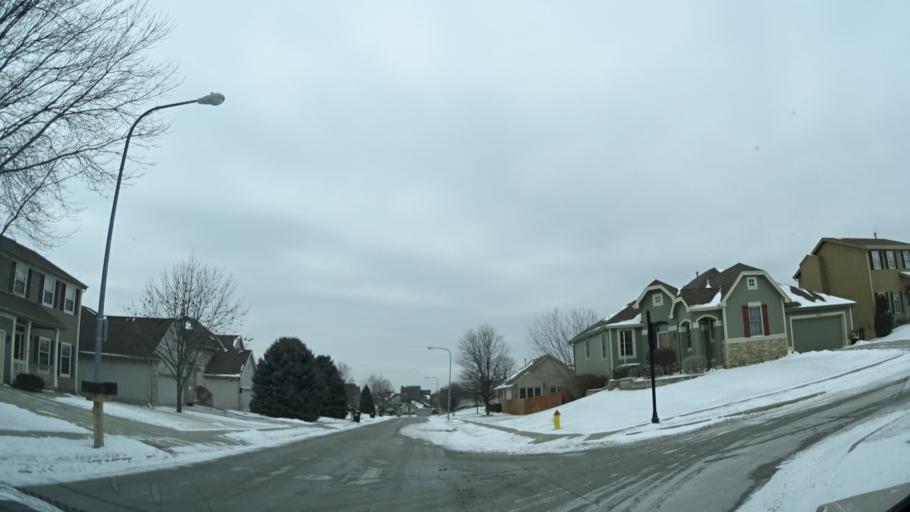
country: US
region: Nebraska
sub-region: Sarpy County
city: Offutt Air Force Base
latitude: 41.1633
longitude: -95.9506
